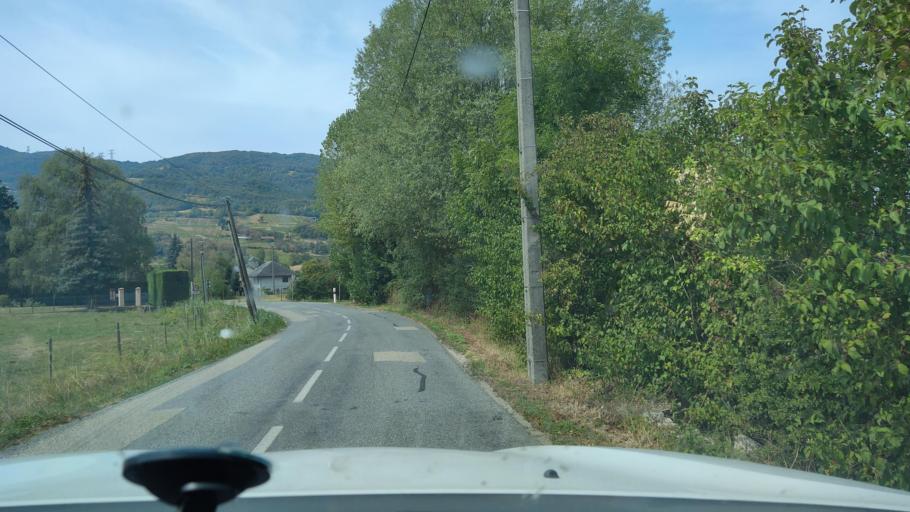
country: FR
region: Rhone-Alpes
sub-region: Departement de la Savoie
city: Saint-Baldoph
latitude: 45.5137
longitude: 5.9659
